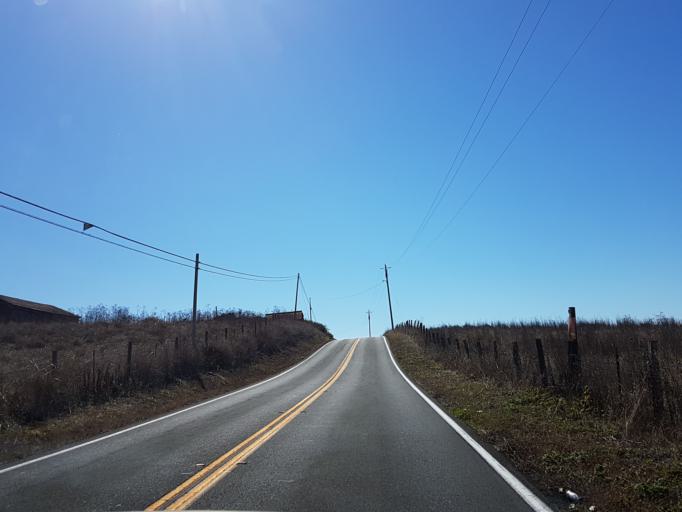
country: US
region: California
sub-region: Mendocino County
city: Boonville
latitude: 39.0719
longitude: -123.6927
